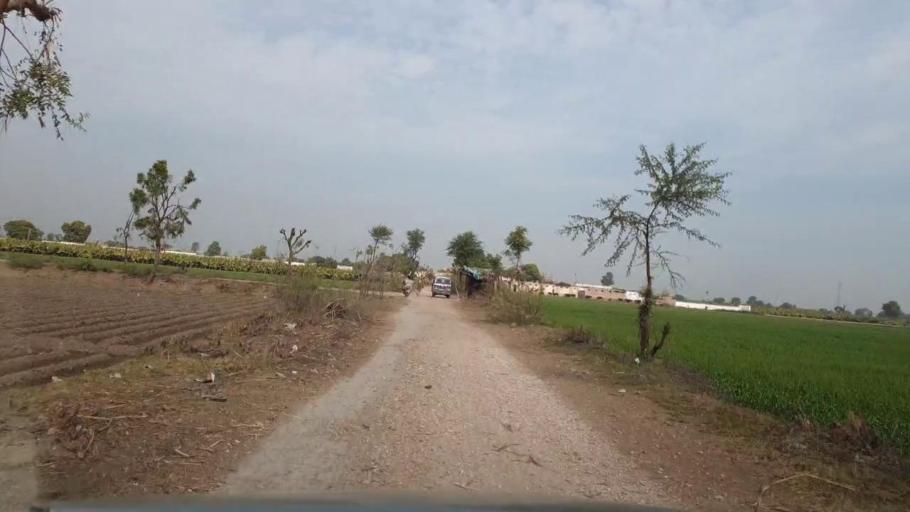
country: PK
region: Sindh
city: Tando Jam
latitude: 25.5277
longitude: 68.5620
